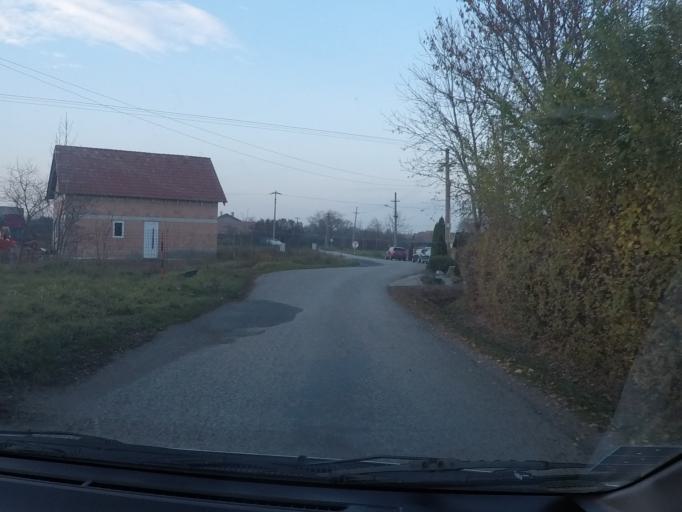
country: SK
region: Nitriansky
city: Zeliezovce
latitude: 48.1011
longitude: 18.5323
